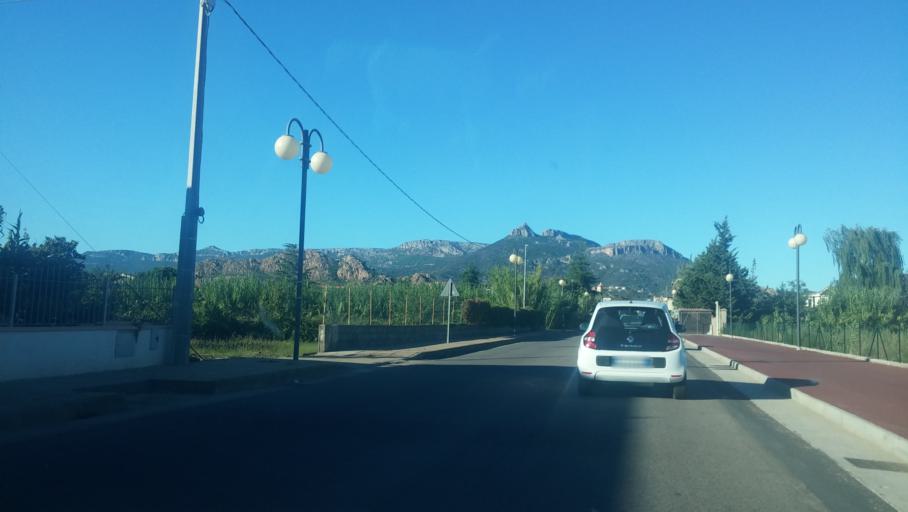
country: IT
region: Sardinia
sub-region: Provincia di Ogliastra
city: Lotzorai
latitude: 39.9661
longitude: 9.6588
